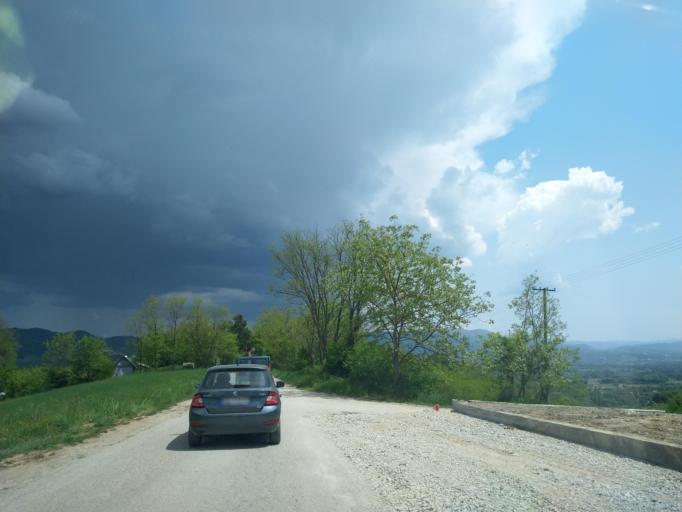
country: RS
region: Central Serbia
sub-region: Zlatiborski Okrug
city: Uzice
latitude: 43.8625
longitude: 19.9362
